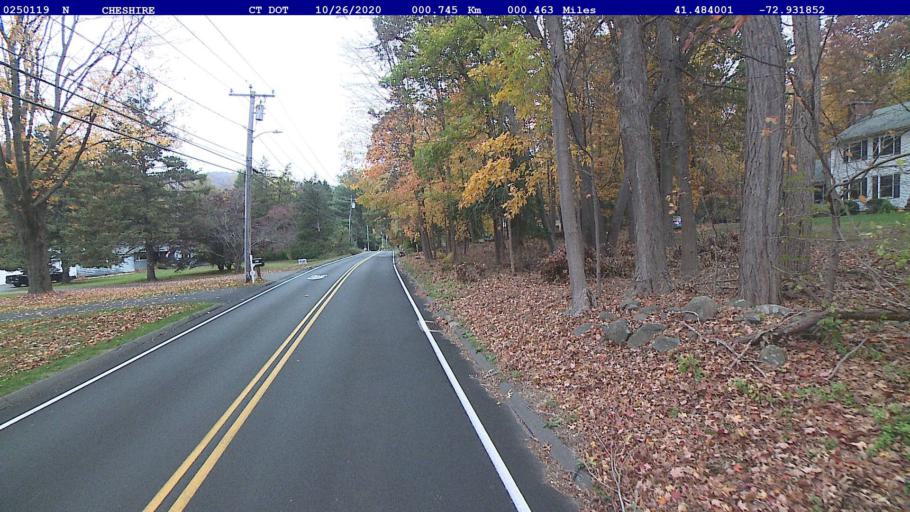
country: US
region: Connecticut
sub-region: New Haven County
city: Cheshire
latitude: 41.4840
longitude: -72.9319
